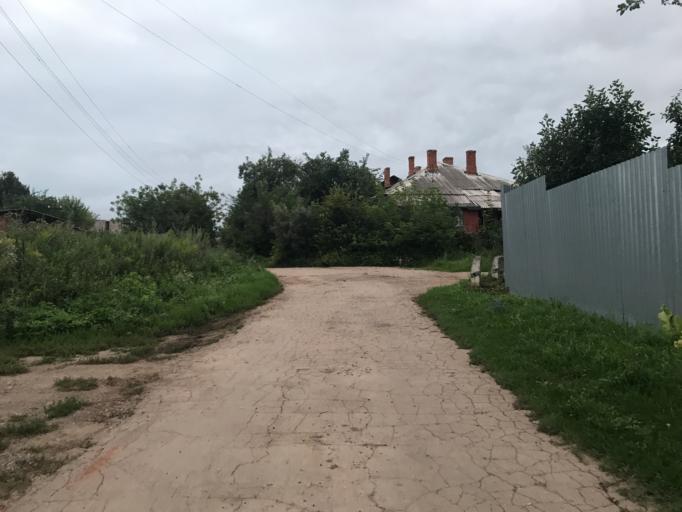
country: RU
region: Tula
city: Priupskiy
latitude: 53.9363
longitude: 37.7085
